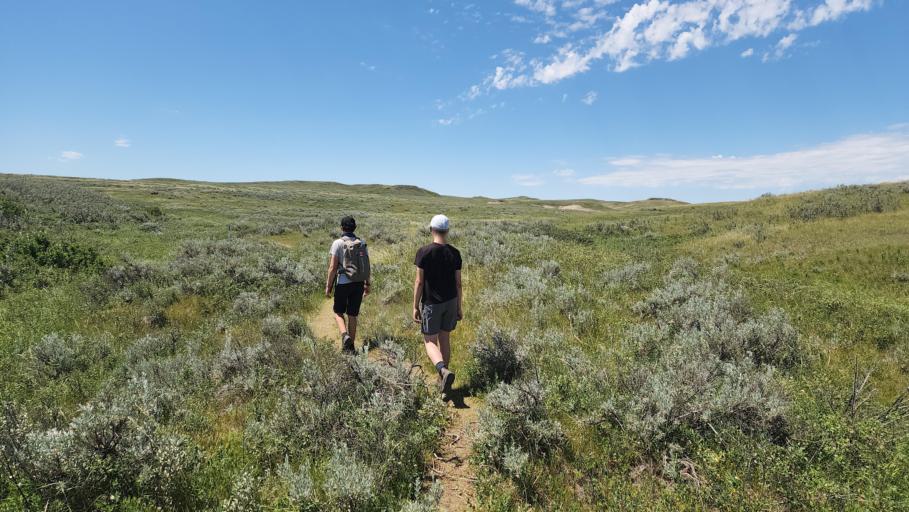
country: CA
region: Saskatchewan
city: Assiniboia
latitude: 49.0666
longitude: -106.5554
